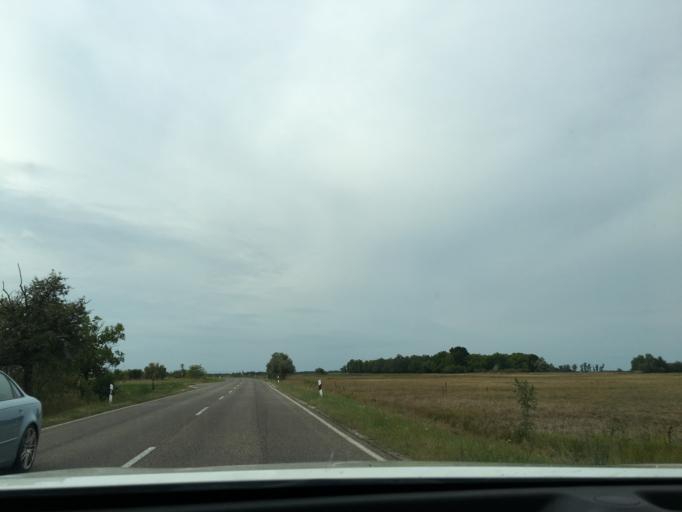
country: HU
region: Hajdu-Bihar
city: Egyek
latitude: 47.5678
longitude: 20.8612
